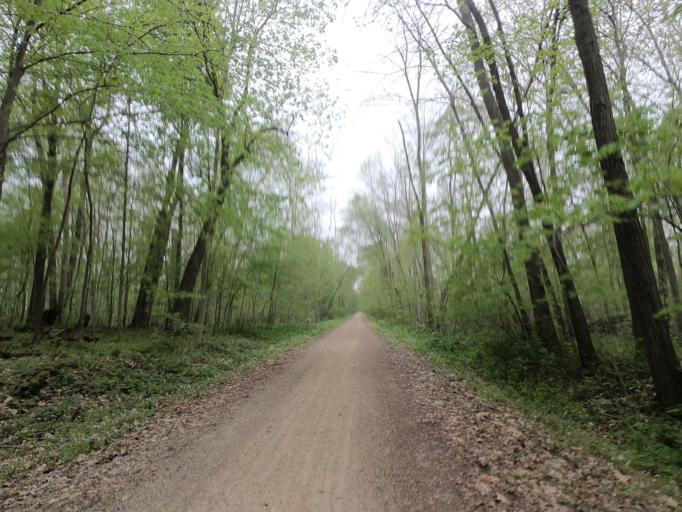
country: US
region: Wisconsin
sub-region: Jefferson County
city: Jefferson
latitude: 43.0394
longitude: -88.8357
